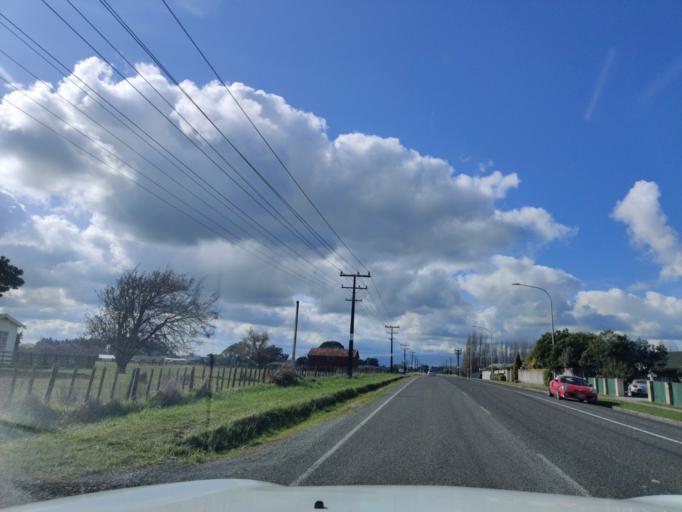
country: NZ
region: Manawatu-Wanganui
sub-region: Palmerston North City
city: Palmerston North
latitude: -40.3194
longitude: 175.6549
